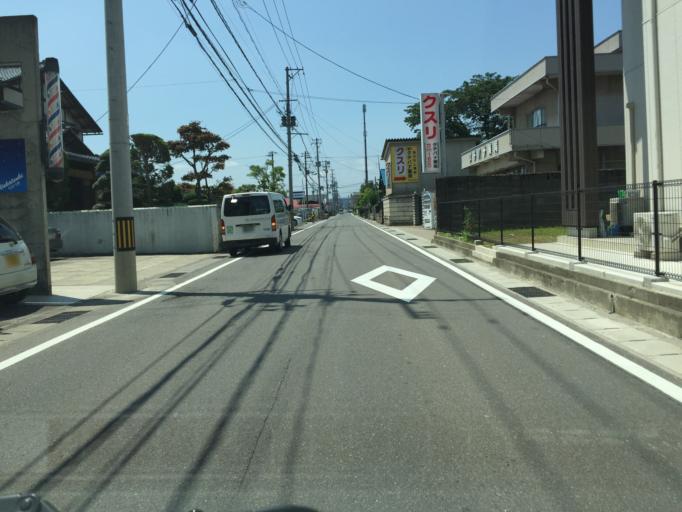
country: JP
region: Fukushima
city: Fukushima-shi
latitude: 37.7466
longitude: 140.4480
